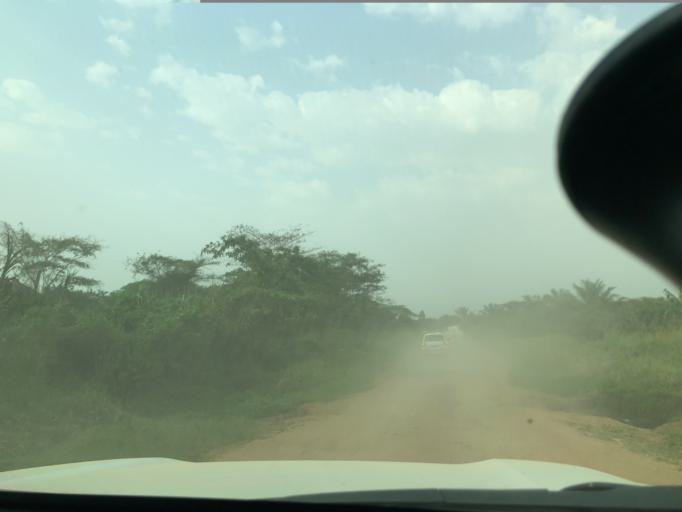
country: UG
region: Western Region
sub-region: Kasese District
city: Margherita
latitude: 0.2069
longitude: 29.6753
